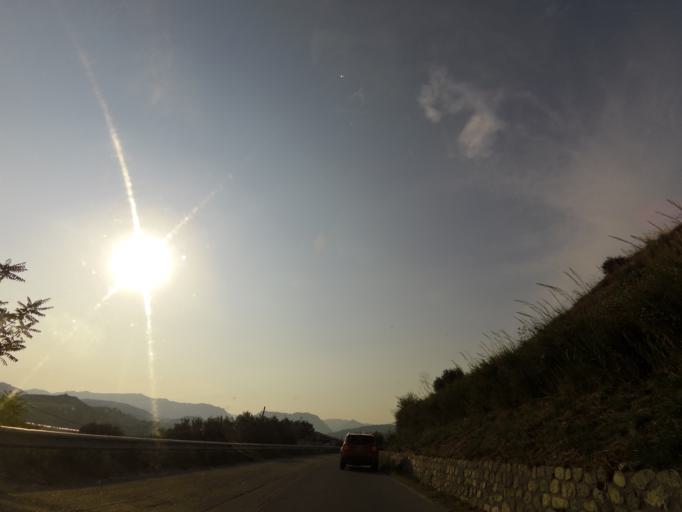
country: IT
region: Calabria
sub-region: Provincia di Reggio Calabria
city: Monasterace
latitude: 38.4534
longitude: 16.5282
